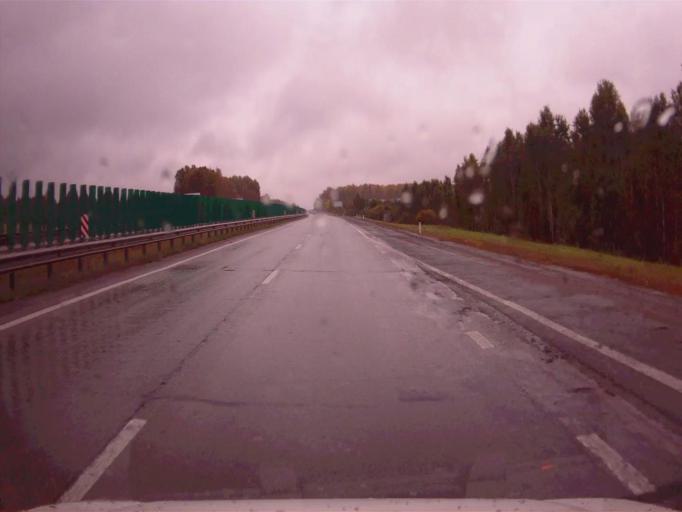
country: RU
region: Chelyabinsk
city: Dolgoderevenskoye
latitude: 55.3281
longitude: 61.3252
